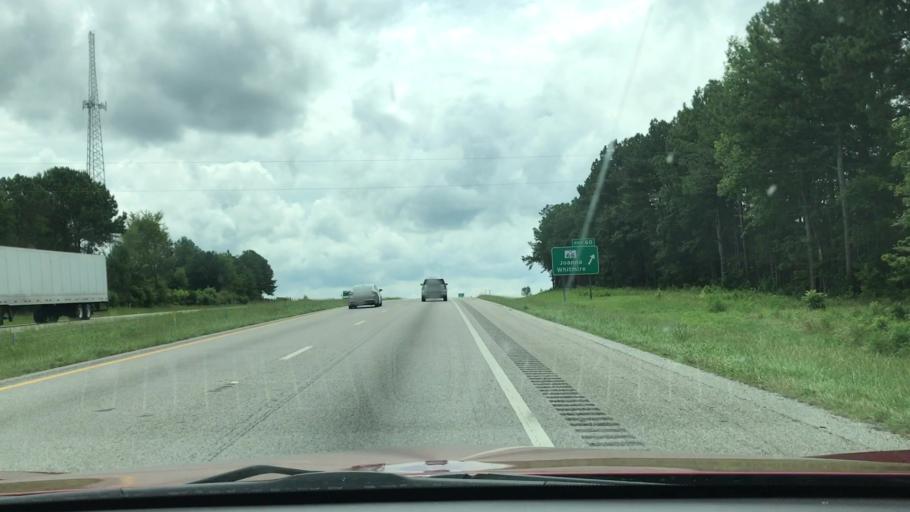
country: US
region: South Carolina
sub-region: Laurens County
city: Joanna
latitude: 34.4421
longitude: -81.7660
